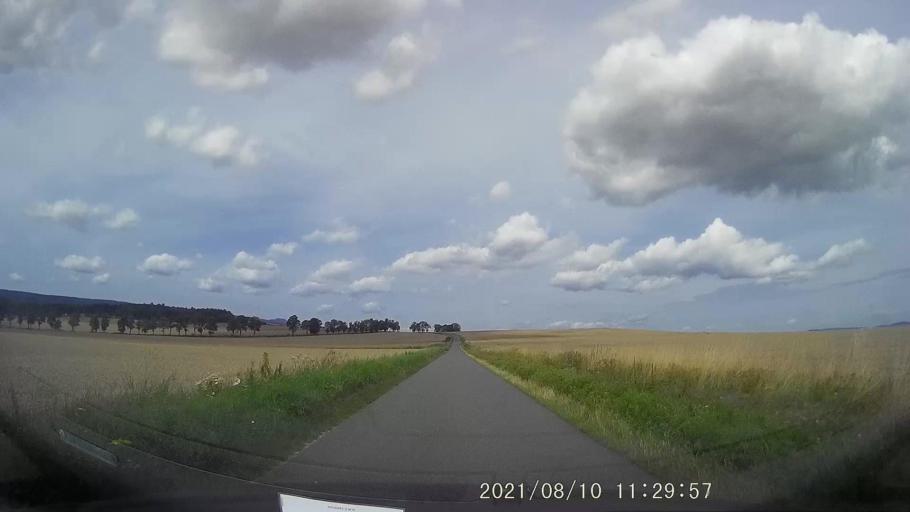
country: PL
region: Lower Silesian Voivodeship
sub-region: Powiat klodzki
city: Polanica-Zdroj
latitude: 50.4476
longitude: 16.5562
